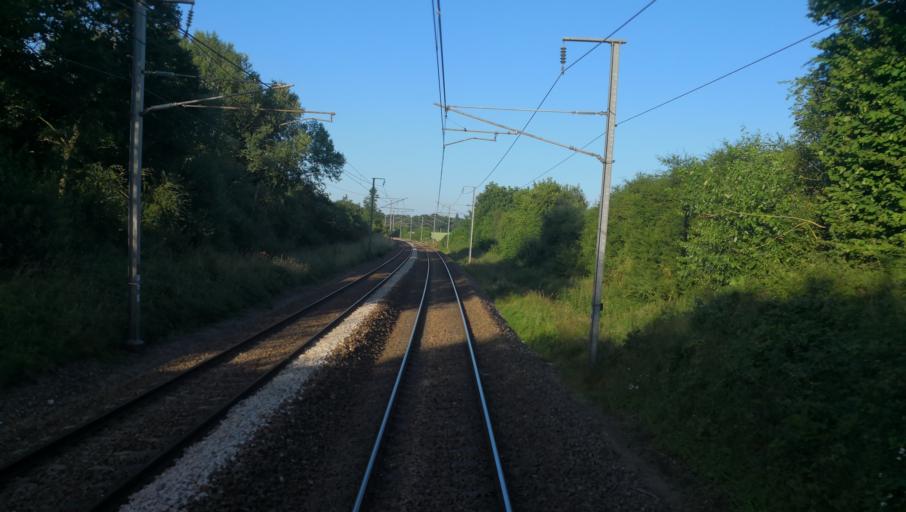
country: FR
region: Haute-Normandie
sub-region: Departement de l'Eure
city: Thiberville
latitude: 49.0812
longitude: 0.5028
